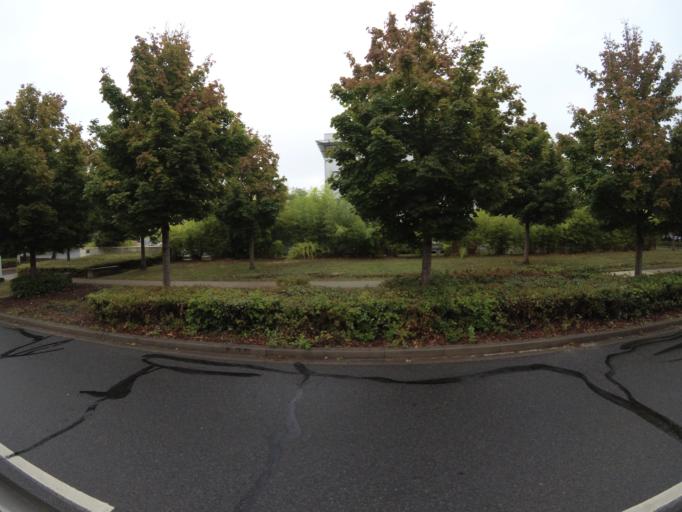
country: FR
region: Ile-de-France
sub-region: Departement de Seine-et-Marne
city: Ferrieres-en-Brie
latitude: 48.8311
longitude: 2.7236
